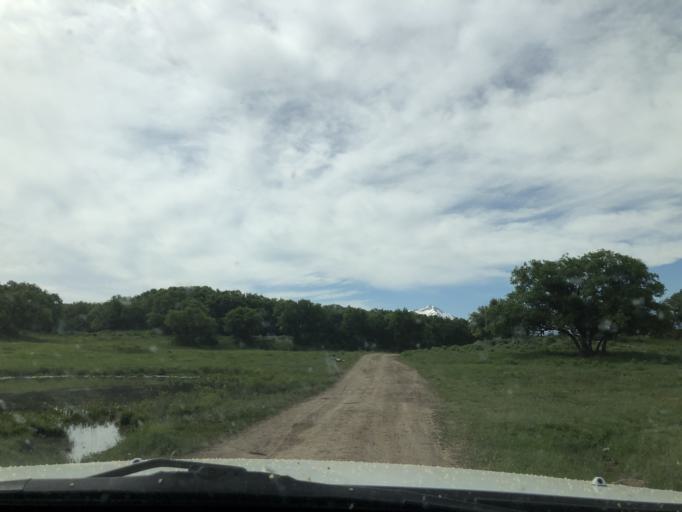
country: US
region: Colorado
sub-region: Delta County
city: Paonia
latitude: 39.0197
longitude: -107.3426
